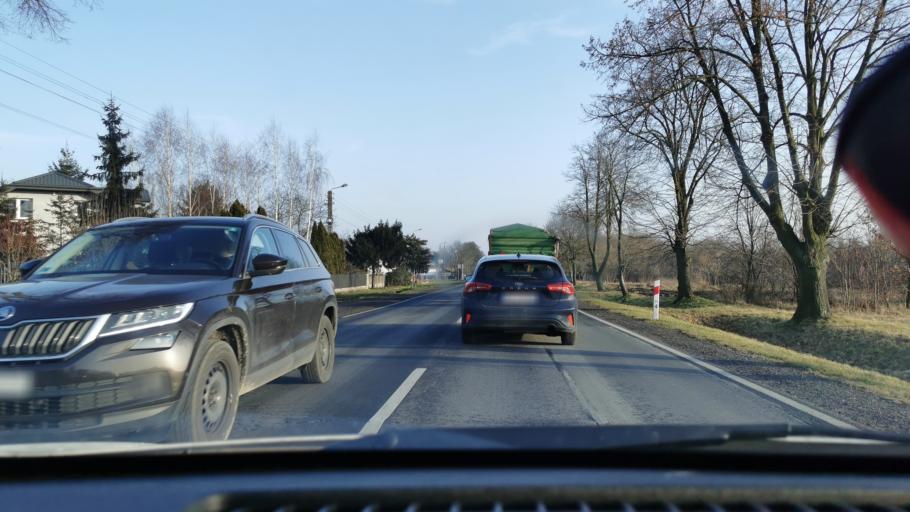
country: PL
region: Lodz Voivodeship
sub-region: Powiat sieradzki
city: Wroblew
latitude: 51.6140
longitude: 18.6083
